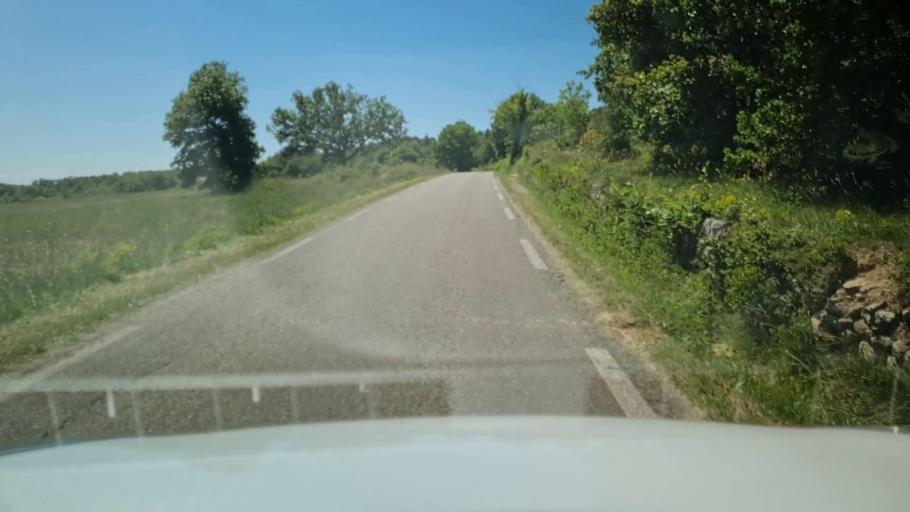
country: FR
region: Languedoc-Roussillon
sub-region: Departement du Gard
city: Saint-Mamert-du-Gard
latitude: 43.8992
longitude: 4.1908
